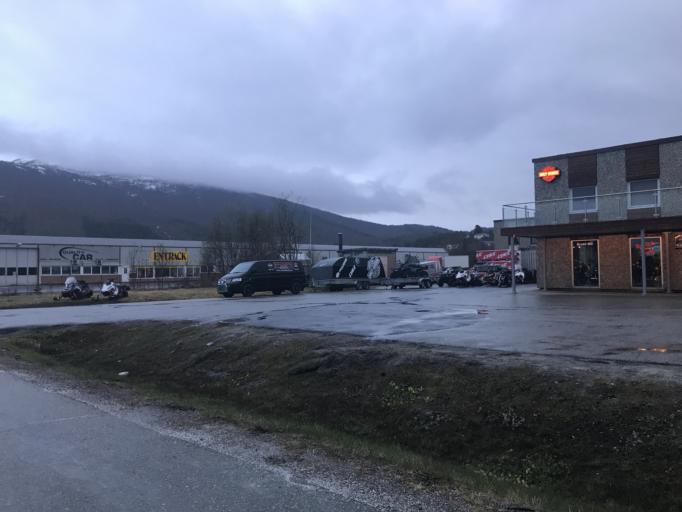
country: NO
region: Nordland
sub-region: Ballangen
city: Ballangen
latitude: 68.3351
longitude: 16.8129
